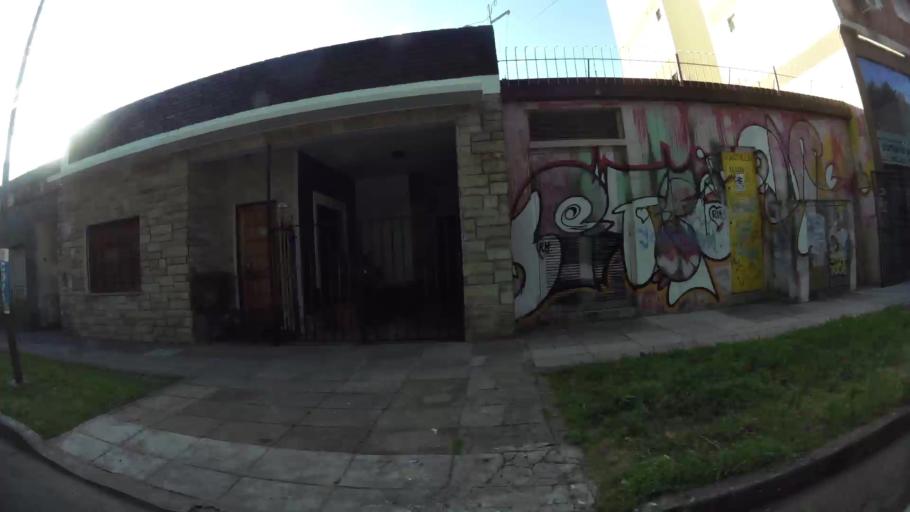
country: AR
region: Buenos Aires
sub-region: Partido de General San Martin
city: General San Martin
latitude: -34.5550
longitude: -58.5579
